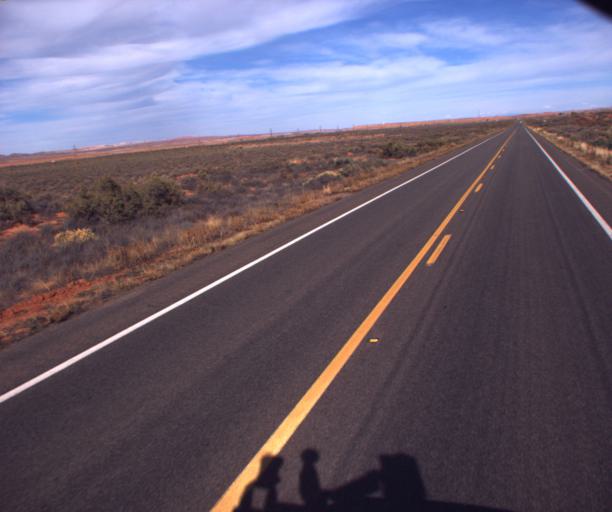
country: US
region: Arizona
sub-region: Navajo County
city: Kayenta
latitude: 36.8033
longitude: -109.9184
